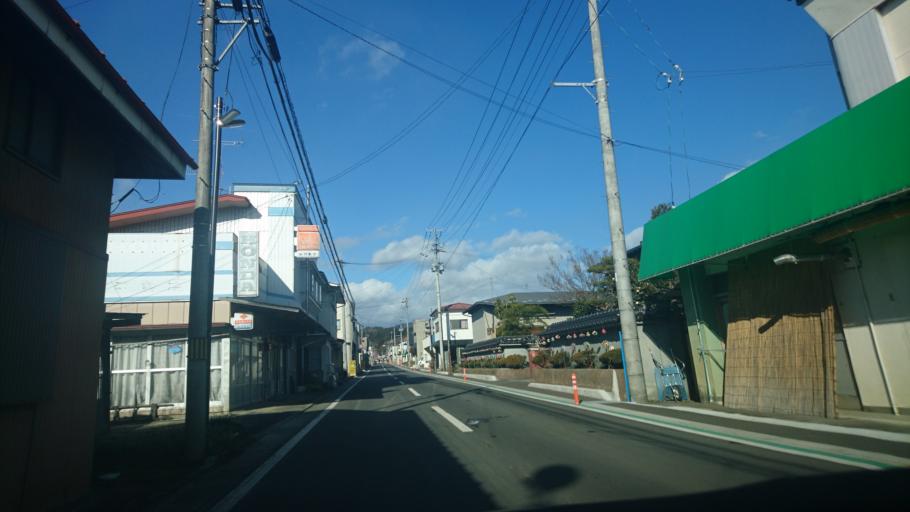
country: JP
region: Iwate
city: Mizusawa
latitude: 39.0493
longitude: 141.3671
